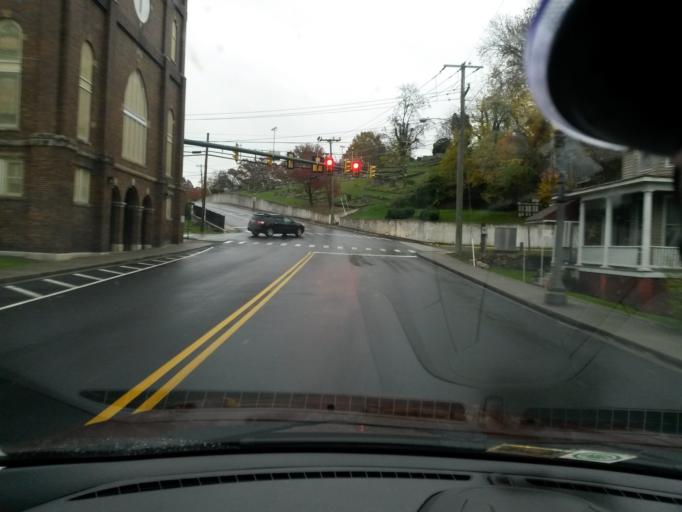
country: US
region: Virginia
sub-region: Alleghany County
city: Clifton Forge
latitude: 37.8152
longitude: -79.8194
